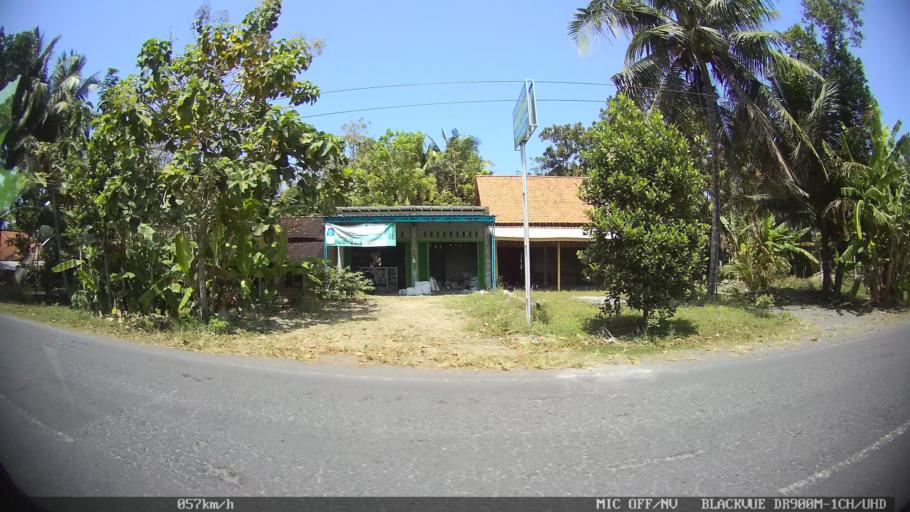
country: ID
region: Daerah Istimewa Yogyakarta
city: Srandakan
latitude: -7.9307
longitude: 110.1380
